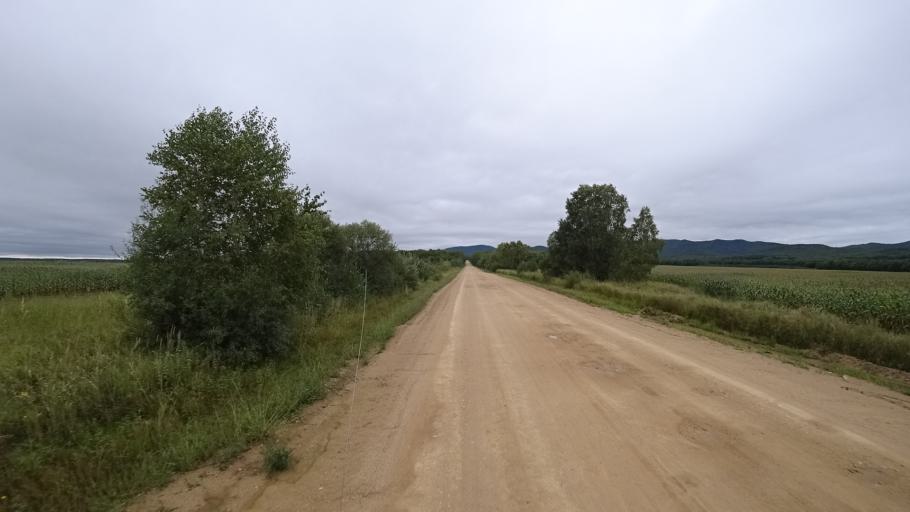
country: RU
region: Primorskiy
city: Rettikhovka
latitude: 44.1592
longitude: 132.7053
